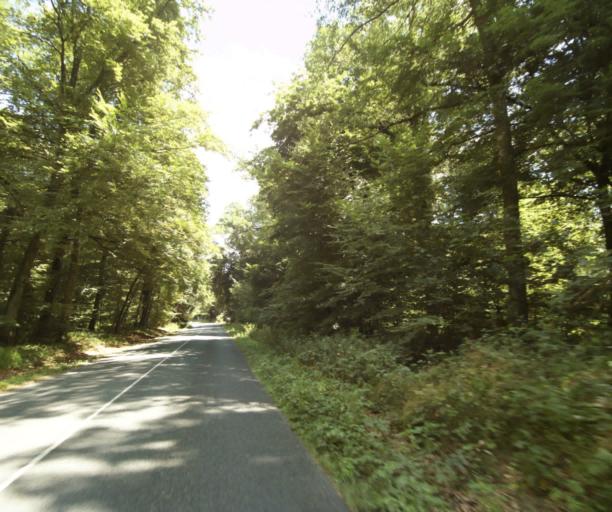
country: FR
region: Ile-de-France
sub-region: Departement de Seine-et-Marne
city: Samois-sur-Seine
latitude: 48.4534
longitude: 2.7356
